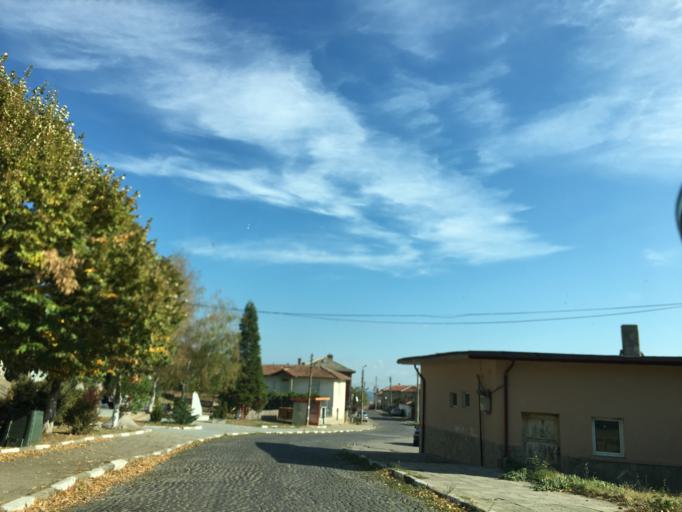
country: BG
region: Khaskovo
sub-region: Obshtina Ivaylovgrad
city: Ivaylovgrad
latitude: 41.5135
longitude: 26.1129
